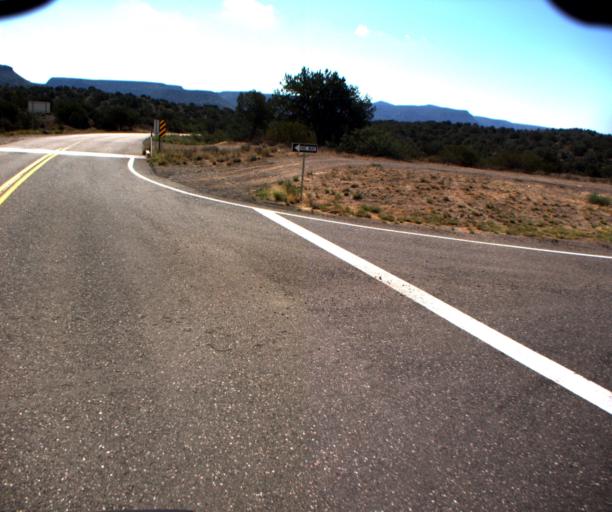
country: US
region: Arizona
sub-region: Yavapai County
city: Lake Montezuma
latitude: 34.6900
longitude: -111.7428
